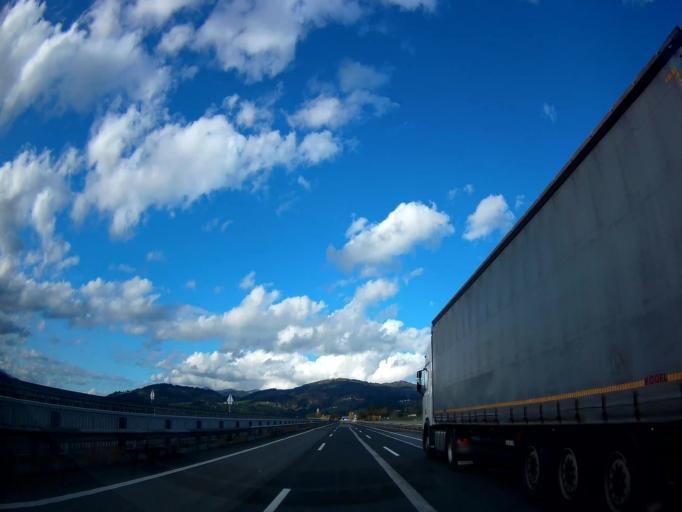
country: AT
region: Carinthia
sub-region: Politischer Bezirk Wolfsberg
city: Bad Sankt Leonhard im Lavanttal
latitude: 46.9188
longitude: 14.8394
